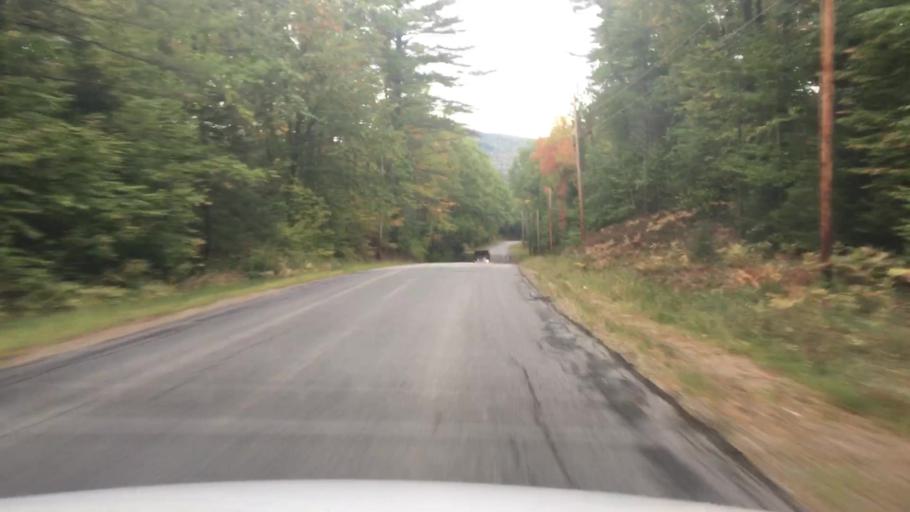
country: US
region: Maine
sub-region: Oxford County
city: Bethel
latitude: 44.4396
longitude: -70.7940
